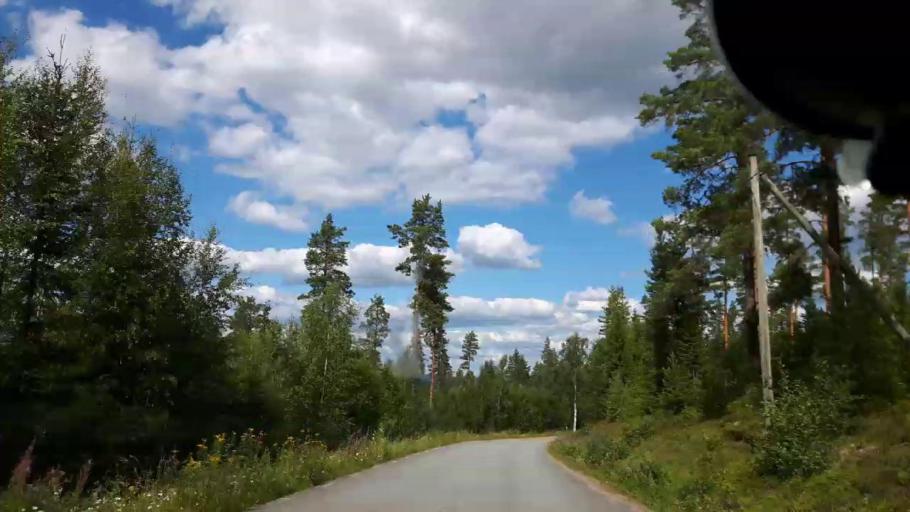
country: SE
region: Jaemtland
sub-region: Ragunda Kommun
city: Hammarstrand
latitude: 62.9325
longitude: 16.6933
